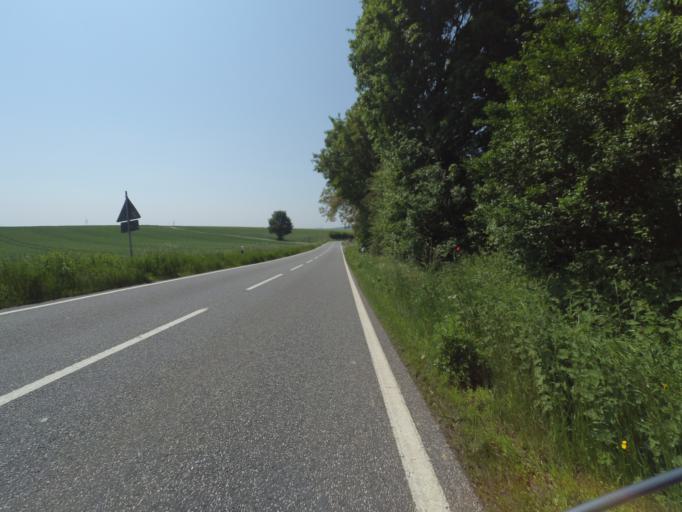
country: DE
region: Rheinland-Pfalz
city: Monreal
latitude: 50.3125
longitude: 7.1869
